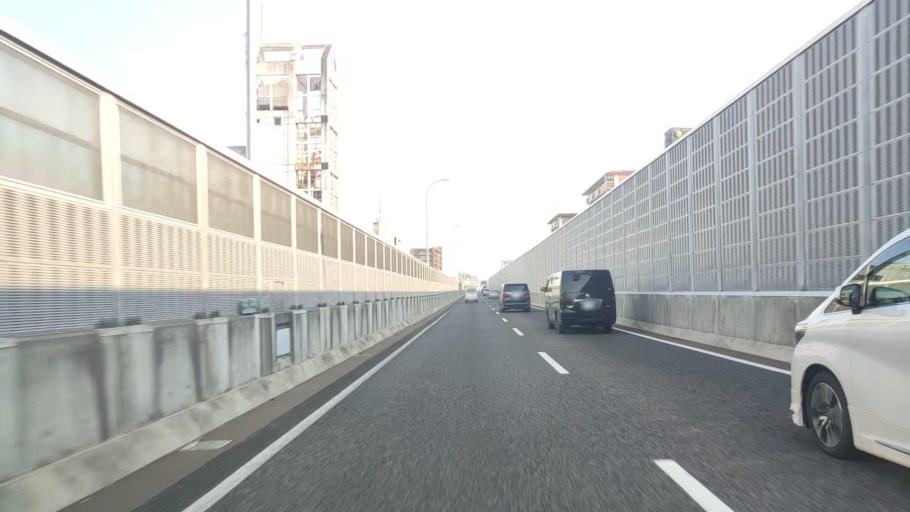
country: JP
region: Aichi
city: Nagoya-shi
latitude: 35.1943
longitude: 136.8908
